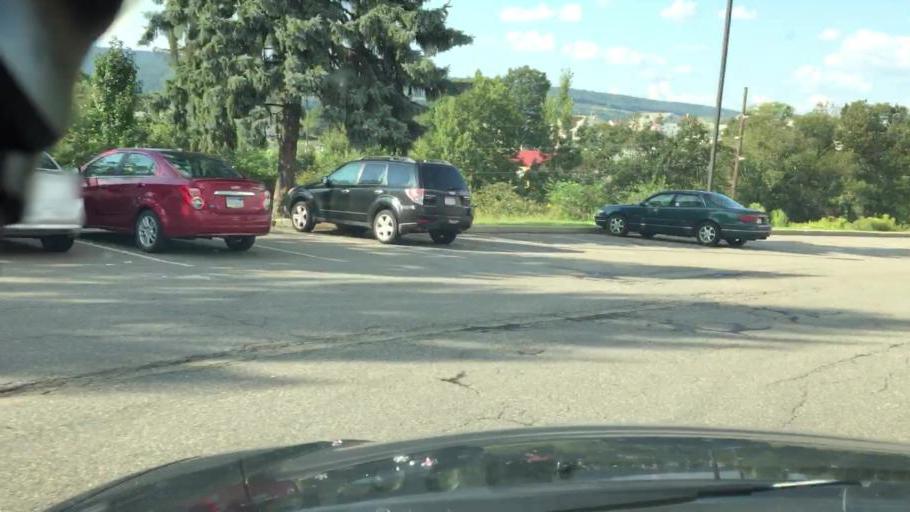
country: US
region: Pennsylvania
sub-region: Luzerne County
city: Nanticoke
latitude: 41.1953
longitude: -75.9927
